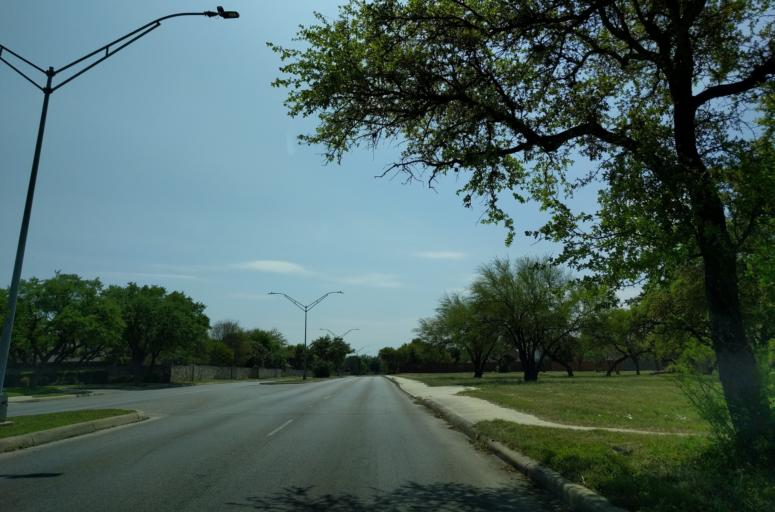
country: US
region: Texas
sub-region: Bexar County
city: Shavano Park
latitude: 29.5719
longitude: -98.5857
